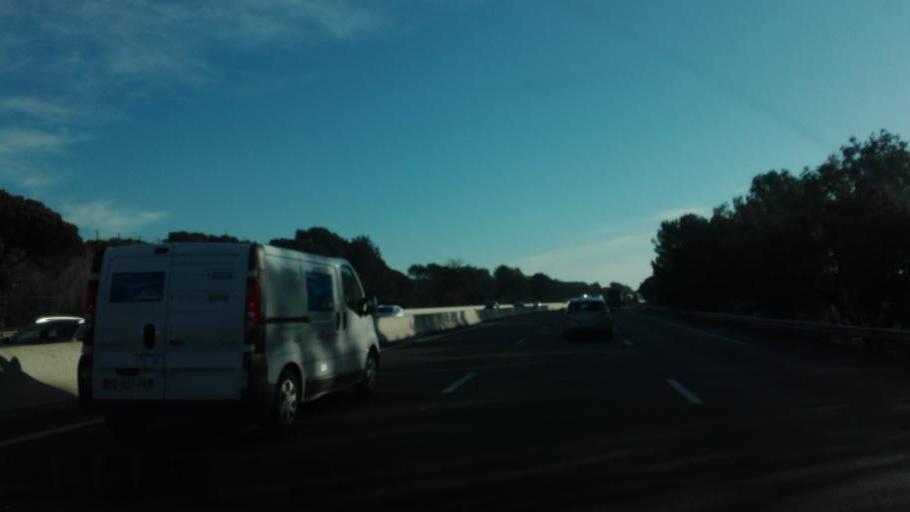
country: FR
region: Provence-Alpes-Cote d'Azur
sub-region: Departement du Var
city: Puget-sur-Argens
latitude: 43.4673
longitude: 6.6622
